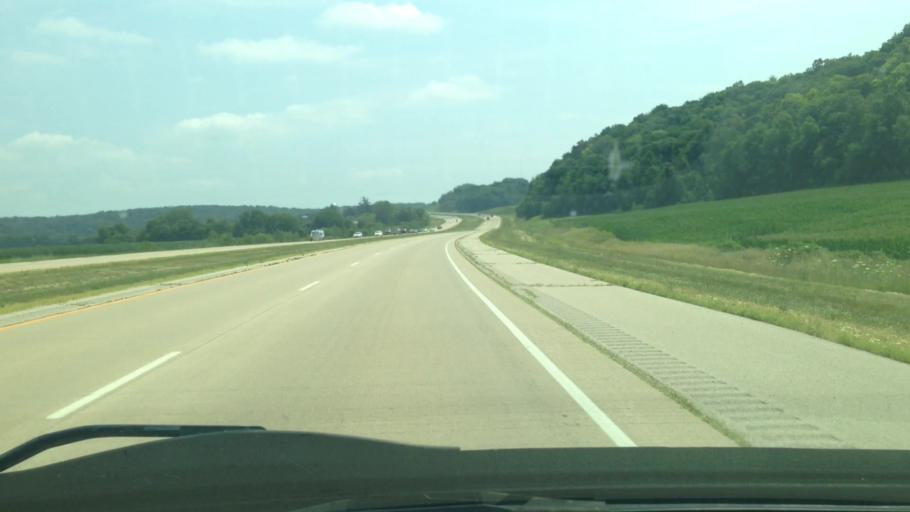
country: US
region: Wisconsin
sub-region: Sauk County
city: Sauk City
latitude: 43.2205
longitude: -89.6344
